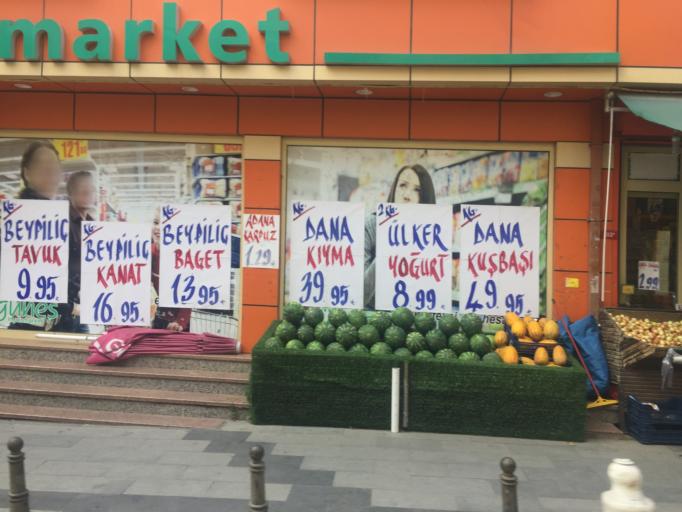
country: TR
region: Istanbul
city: Esenler
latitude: 41.0498
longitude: 28.9066
